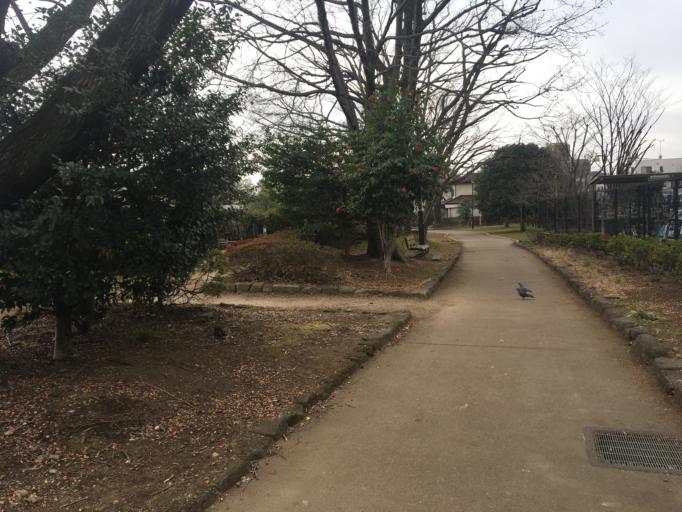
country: JP
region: Tokyo
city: Musashino
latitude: 35.7160
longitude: 139.5549
